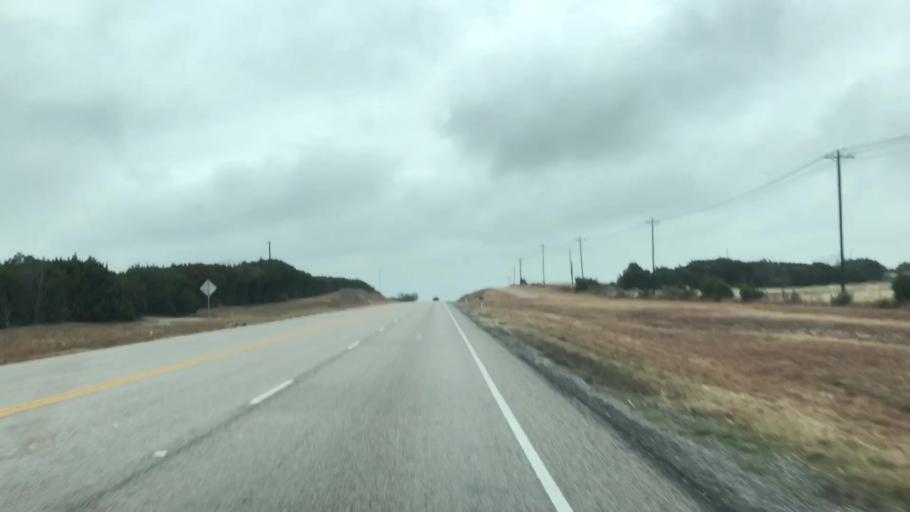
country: US
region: Texas
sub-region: Lampasas County
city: Lampasas
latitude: 30.9392
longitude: -98.2311
